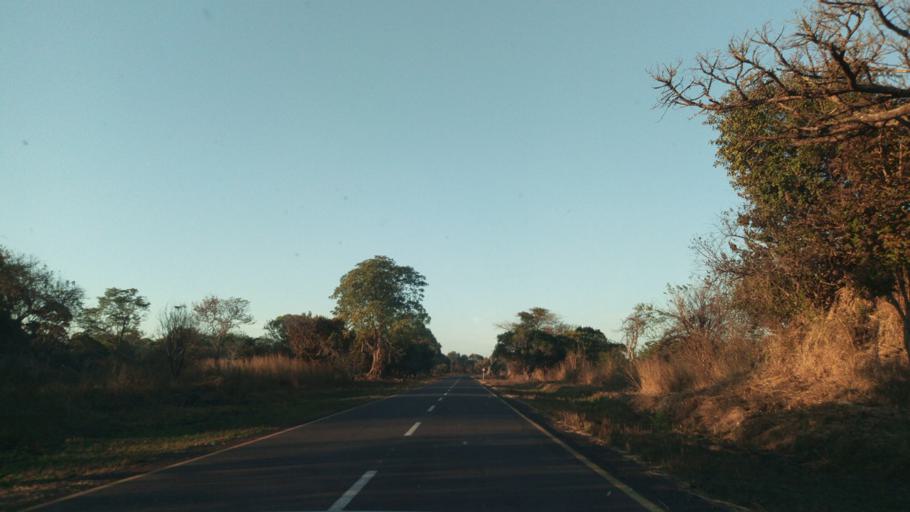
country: ZM
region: Luapula
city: Mwense
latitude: -10.7698
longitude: 28.2599
